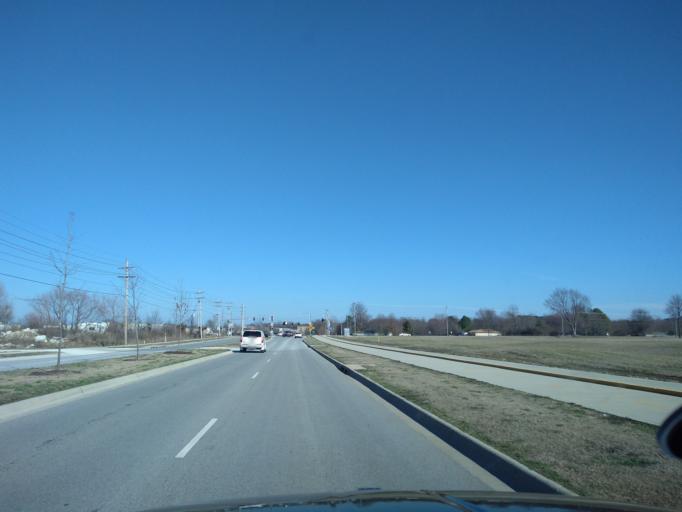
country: US
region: Arkansas
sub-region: Washington County
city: Johnson
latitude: 36.1170
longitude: -94.1662
